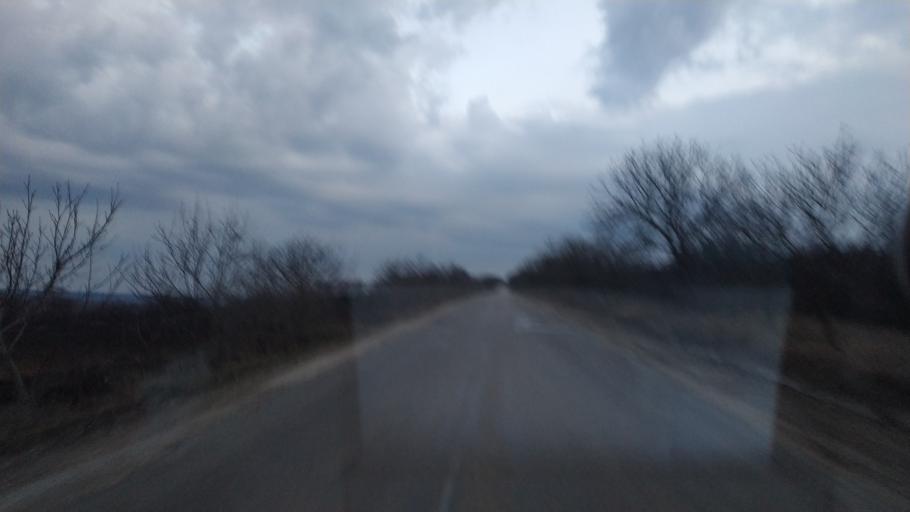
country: MD
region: Anenii Noi
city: Anenii Noi
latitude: 46.9421
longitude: 29.2841
